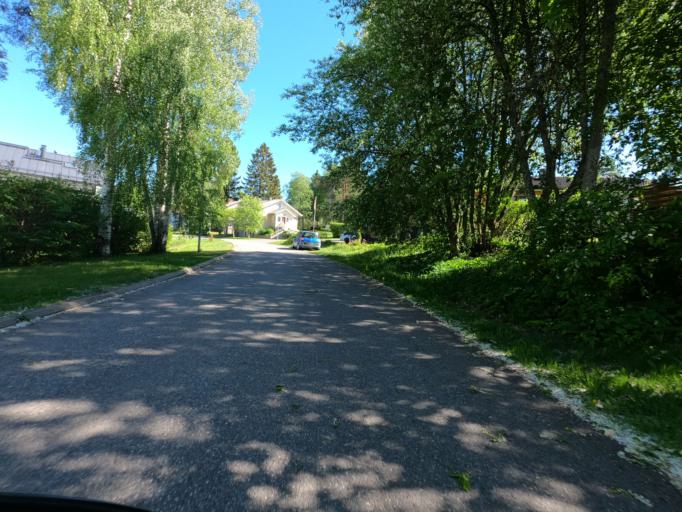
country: FI
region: North Karelia
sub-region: Joensuu
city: Joensuu
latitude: 62.5924
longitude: 29.7933
